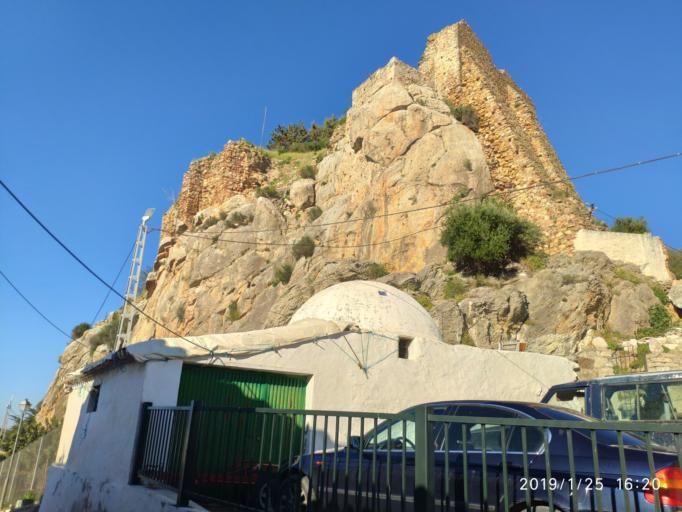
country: ES
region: Andalusia
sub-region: Provincia de Malaga
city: Ardales
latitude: 36.8758
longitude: -4.8448
